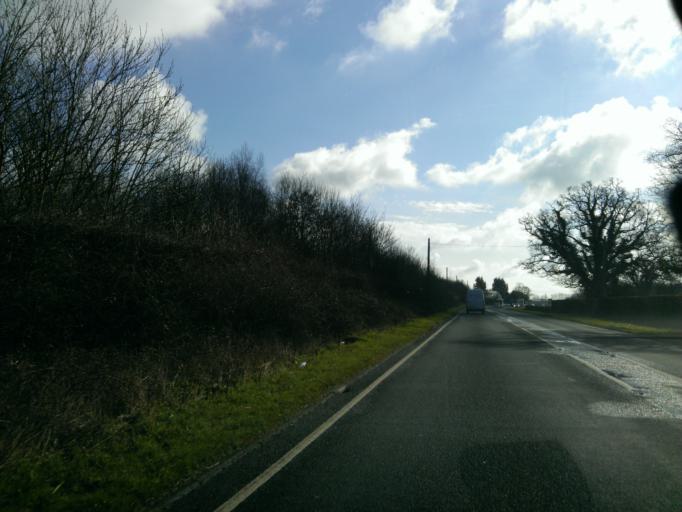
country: GB
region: England
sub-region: Essex
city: Great Bentley
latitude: 51.8638
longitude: 1.0867
